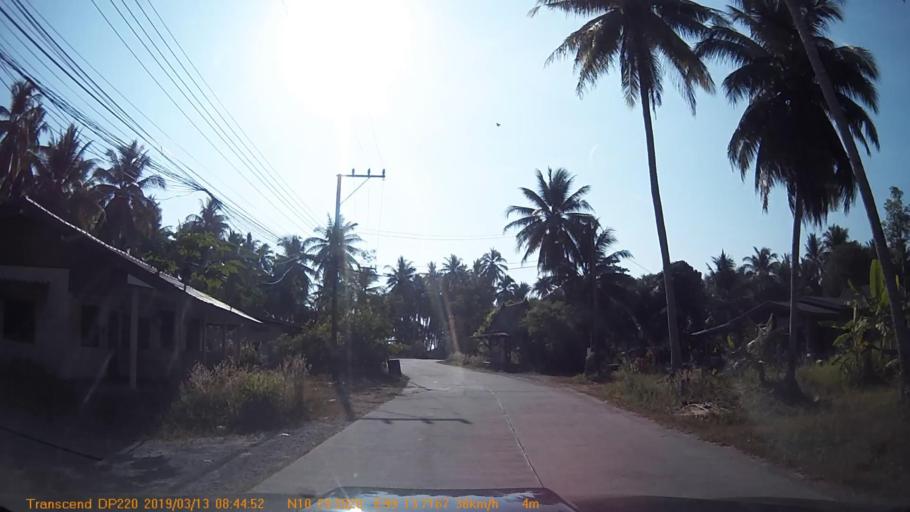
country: TH
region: Chumphon
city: Chumphon
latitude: 10.4931
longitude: 99.2287
